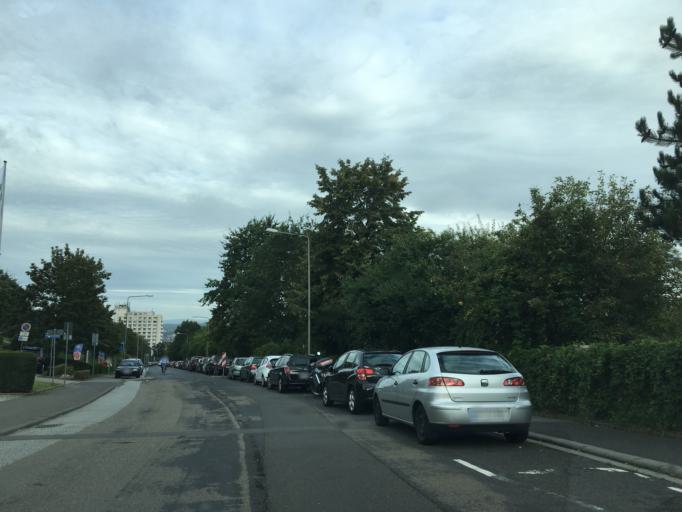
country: DE
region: Hesse
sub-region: Regierungsbezirk Darmstadt
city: Wiesbaden
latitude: 50.0878
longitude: 8.2748
